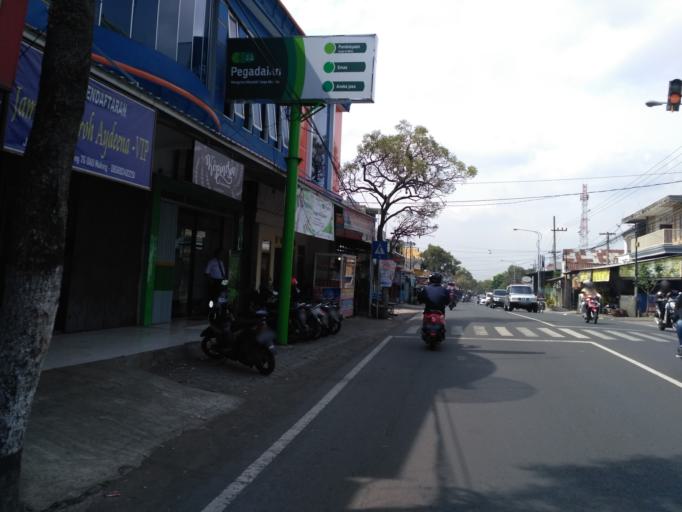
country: ID
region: East Java
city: Malang
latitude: -7.9189
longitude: 112.5911
